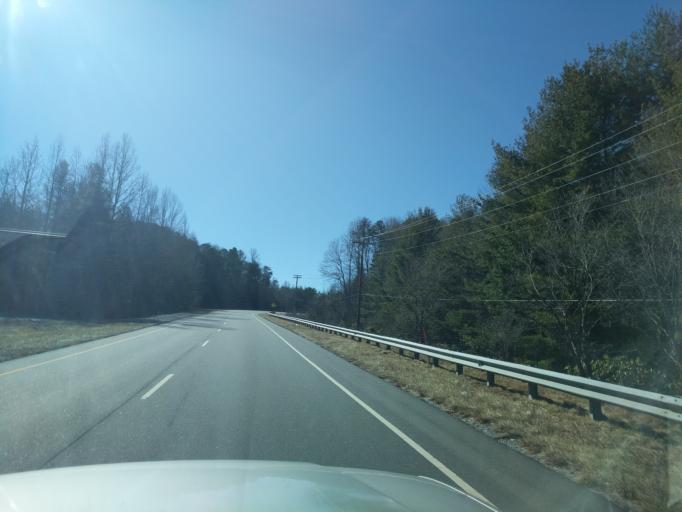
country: US
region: North Carolina
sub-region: Swain County
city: Bryson City
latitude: 35.3892
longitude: -83.4834
